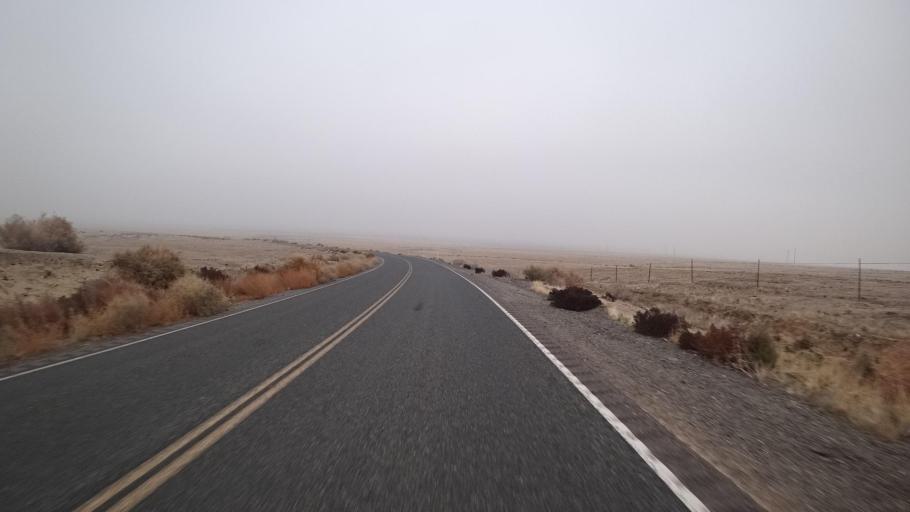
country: US
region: California
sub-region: Kern County
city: Buttonwillow
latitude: 35.3290
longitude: -119.4636
